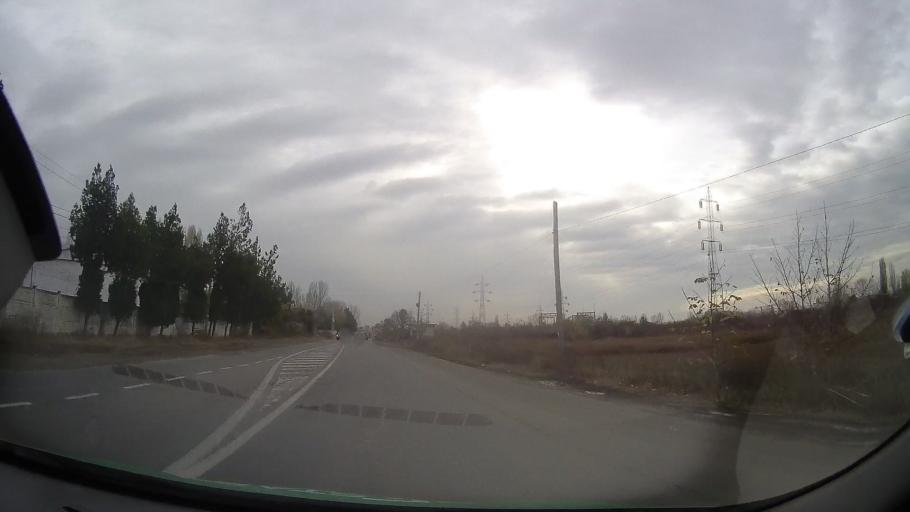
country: RO
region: Prahova
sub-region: Comuna Berceni
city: Berceni
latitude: 44.9455
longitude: 26.1002
